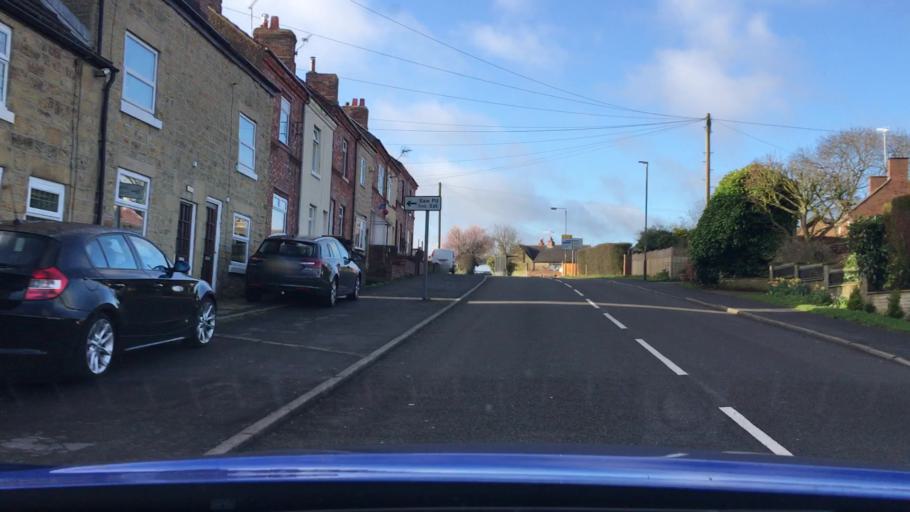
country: GB
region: England
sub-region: Derbyshire
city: Tibshelf
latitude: 53.1486
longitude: -1.3358
